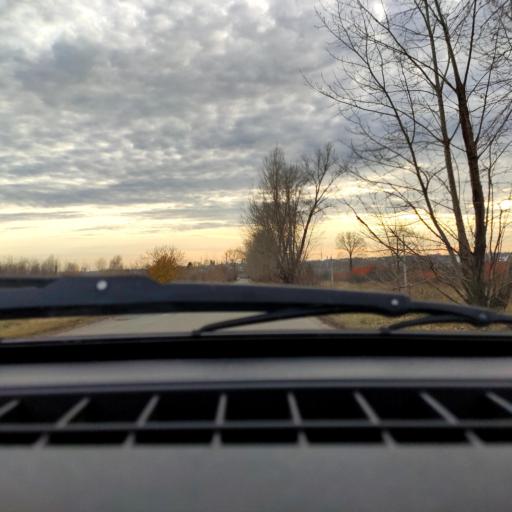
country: RU
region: Bashkortostan
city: Ufa
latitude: 54.8822
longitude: 56.1338
